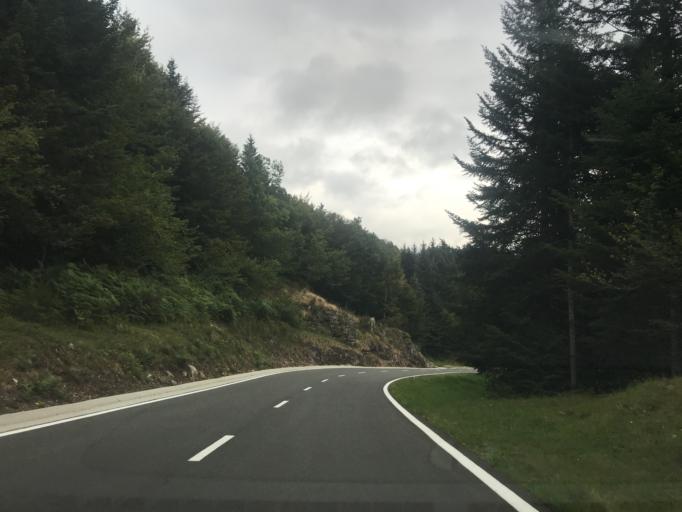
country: ES
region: Catalonia
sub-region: Provincia de Lleida
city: Les
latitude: 42.7681
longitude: 0.6672
